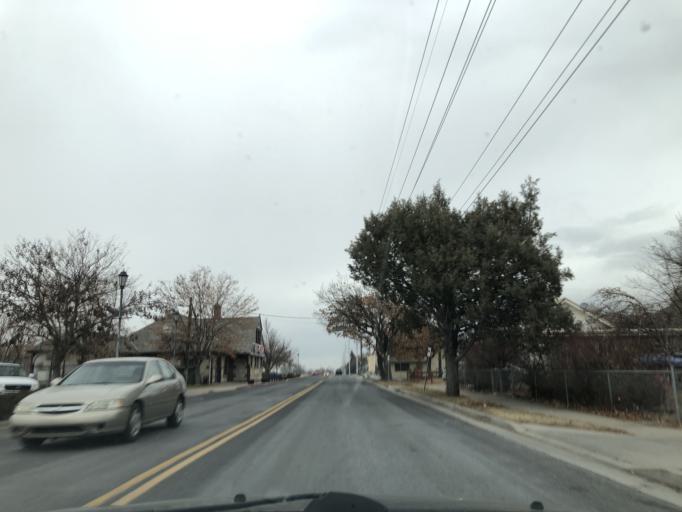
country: US
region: Utah
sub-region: Cache County
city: Logan
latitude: 41.7309
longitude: -111.8498
